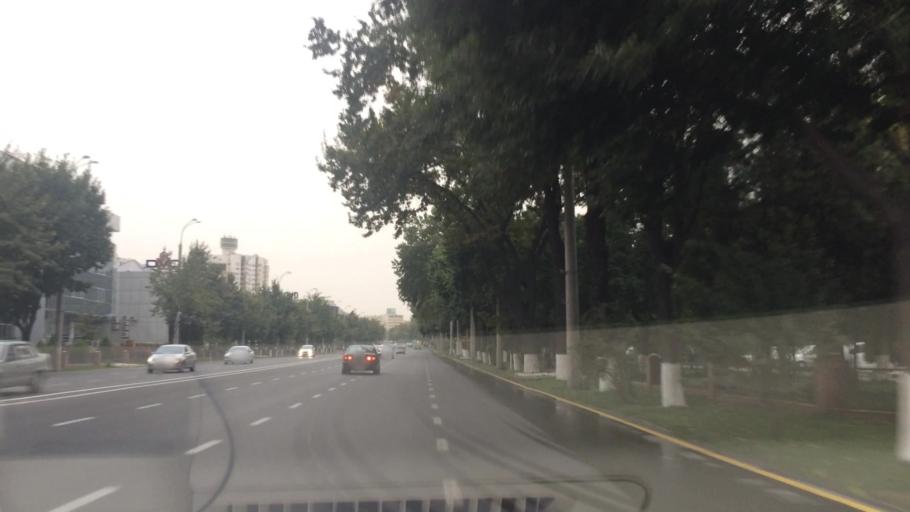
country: UZ
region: Toshkent Shahri
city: Tashkent
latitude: 41.2995
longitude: 69.2726
